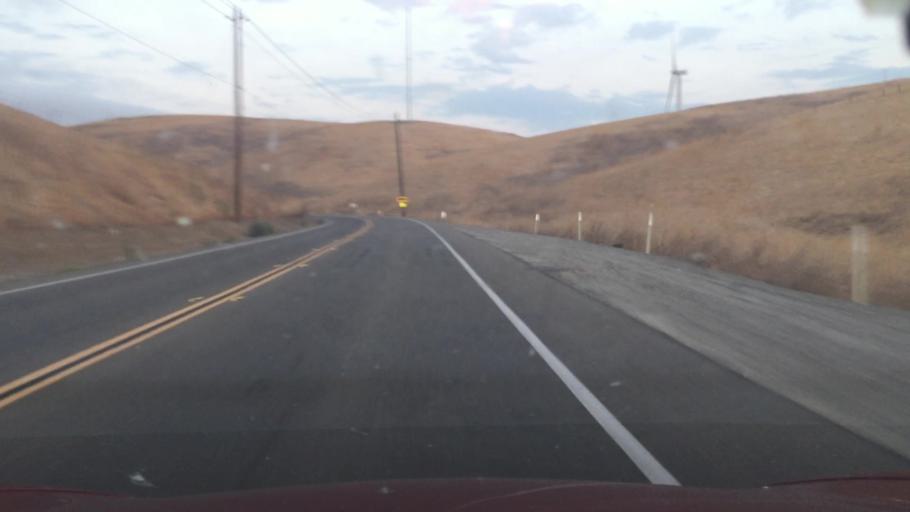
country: US
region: California
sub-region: San Joaquin County
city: Mountain House
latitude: 37.7430
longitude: -121.6253
